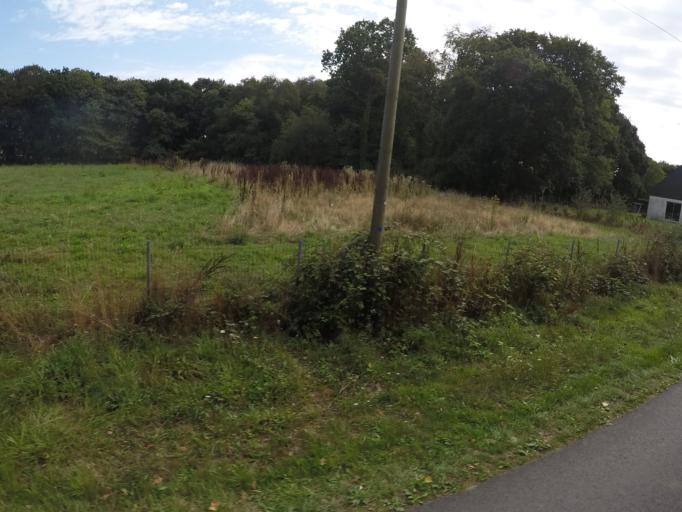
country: FR
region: Brittany
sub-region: Departement des Cotes-d'Armor
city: Lanvollon
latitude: 48.6403
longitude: -2.9940
